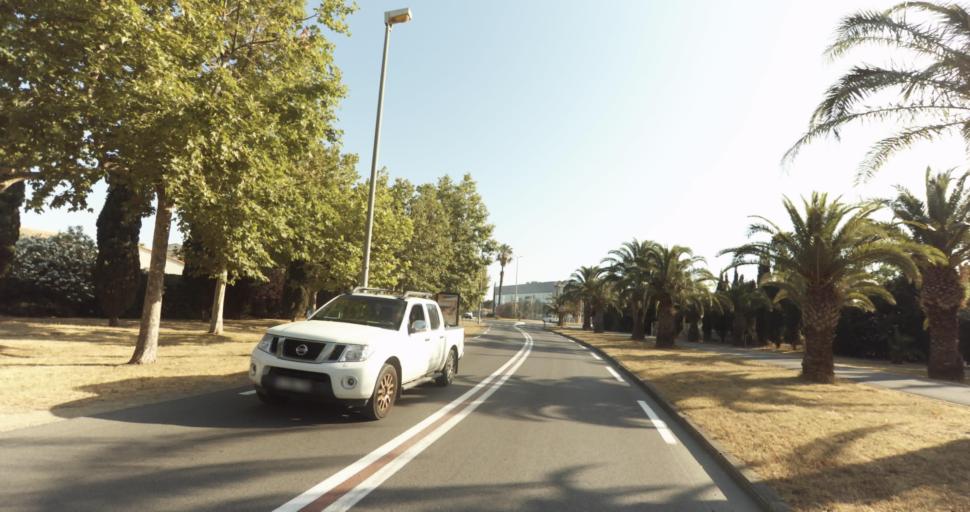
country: FR
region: Languedoc-Roussillon
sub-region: Departement des Pyrenees-Orientales
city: Saint-Cyprien-Plage
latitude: 42.6140
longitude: 3.0336
